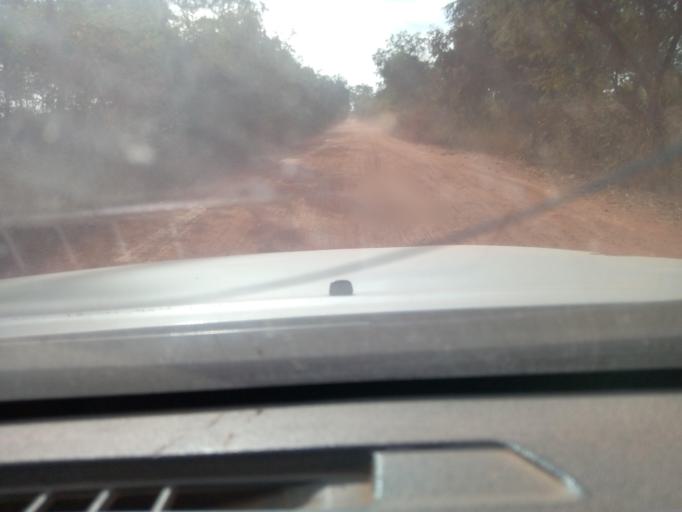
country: ML
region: Sikasso
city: Sikasso
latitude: 11.9360
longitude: -6.0762
